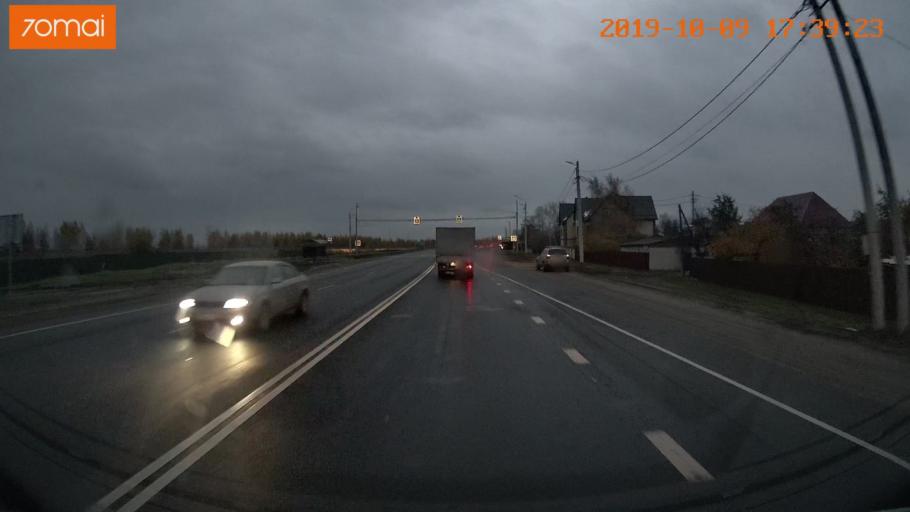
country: RU
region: Ivanovo
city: Bogorodskoye
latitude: 57.0610
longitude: 40.9579
